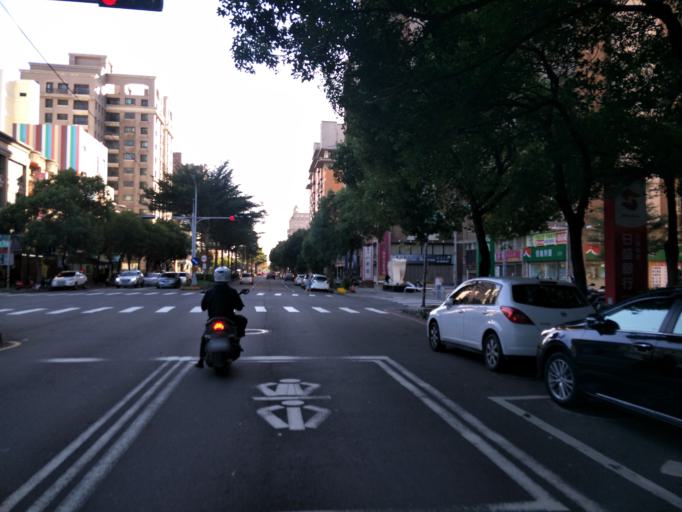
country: TW
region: Taiwan
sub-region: Hsinchu
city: Zhubei
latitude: 24.8339
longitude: 121.0193
